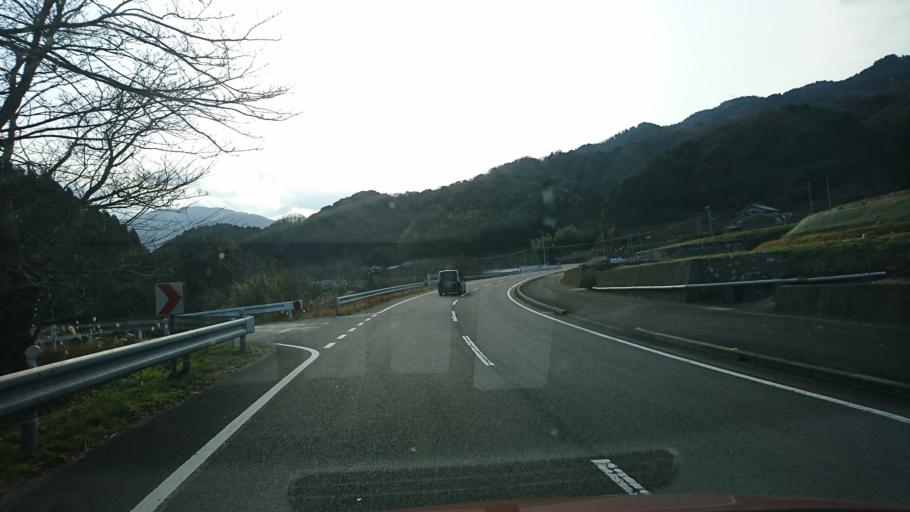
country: JP
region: Ehime
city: Hojo
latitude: 33.9882
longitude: 132.9105
